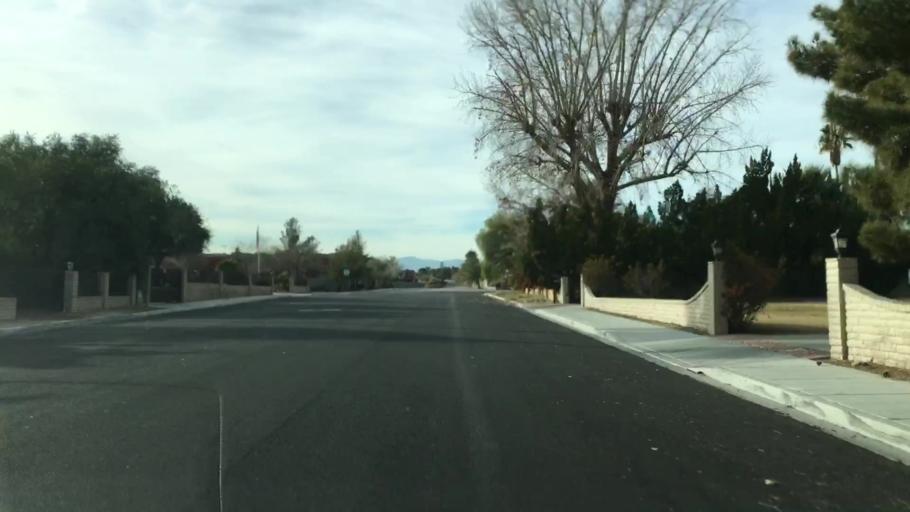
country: US
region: Nevada
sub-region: Clark County
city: Whitney
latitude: 36.0824
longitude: -115.0953
